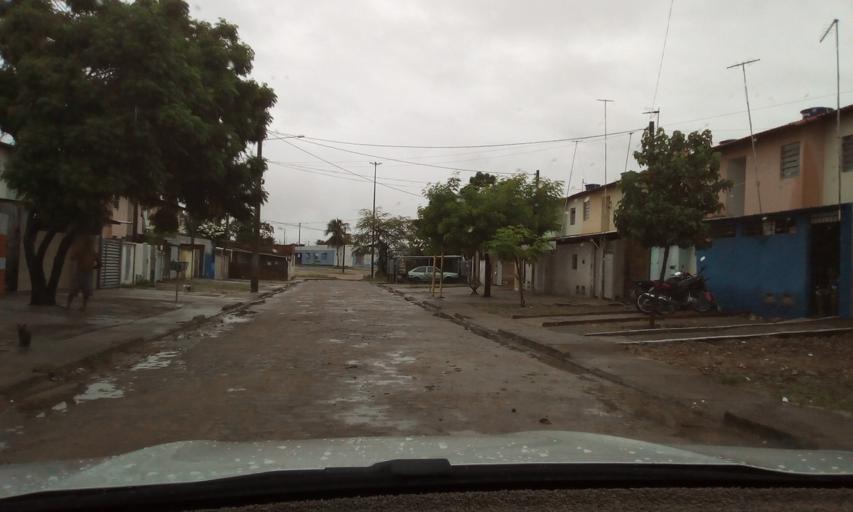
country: BR
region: Paraiba
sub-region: Conde
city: Conde
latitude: -7.2103
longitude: -34.8379
